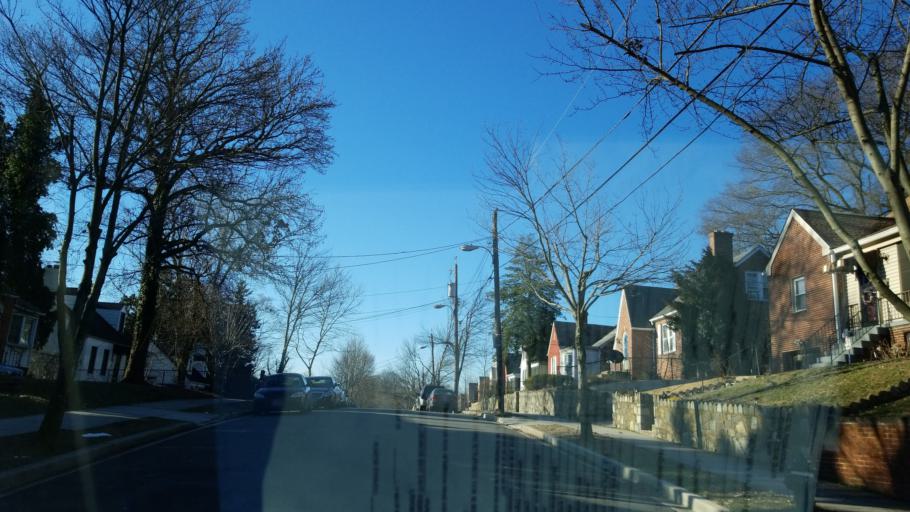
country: US
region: Maryland
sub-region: Prince George's County
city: Glassmanor
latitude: 38.8334
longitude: -77.0097
